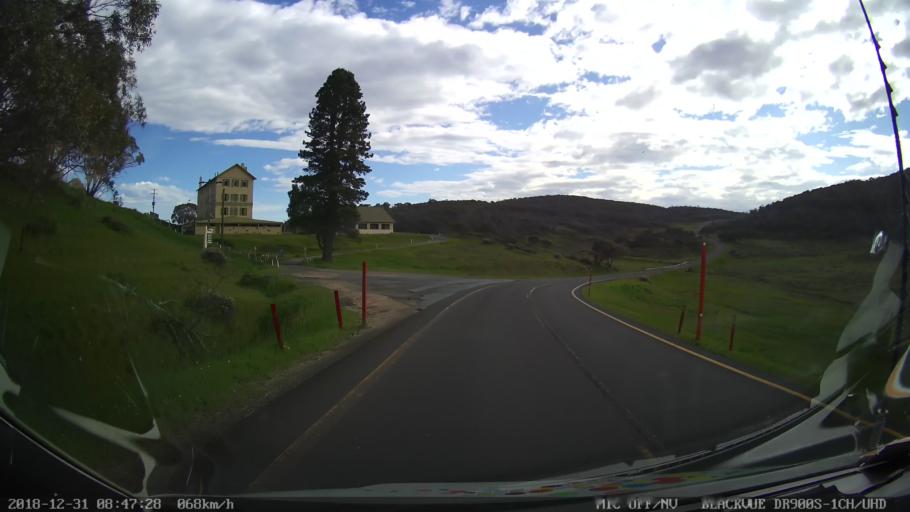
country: AU
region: New South Wales
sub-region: Snowy River
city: Jindabyne
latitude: -36.3612
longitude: 148.4846
